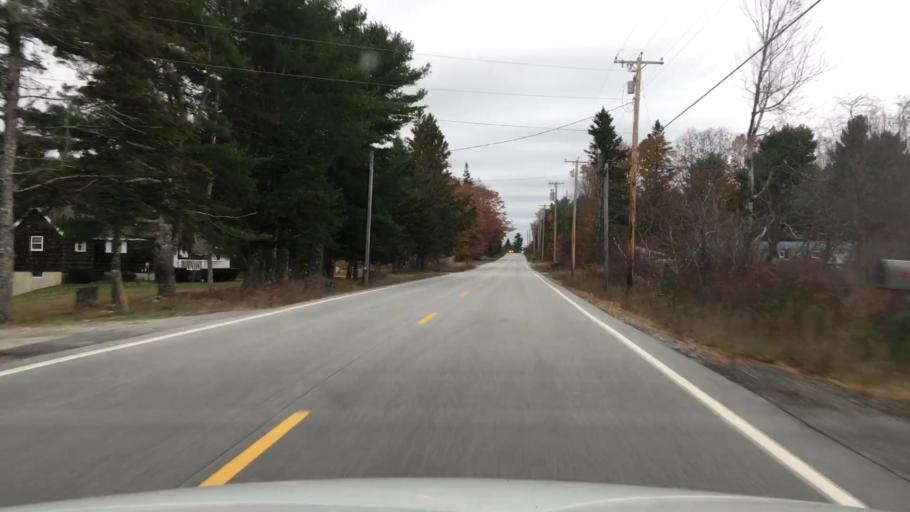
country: US
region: Maine
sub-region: Hancock County
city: Orland
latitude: 44.5425
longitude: -68.6851
